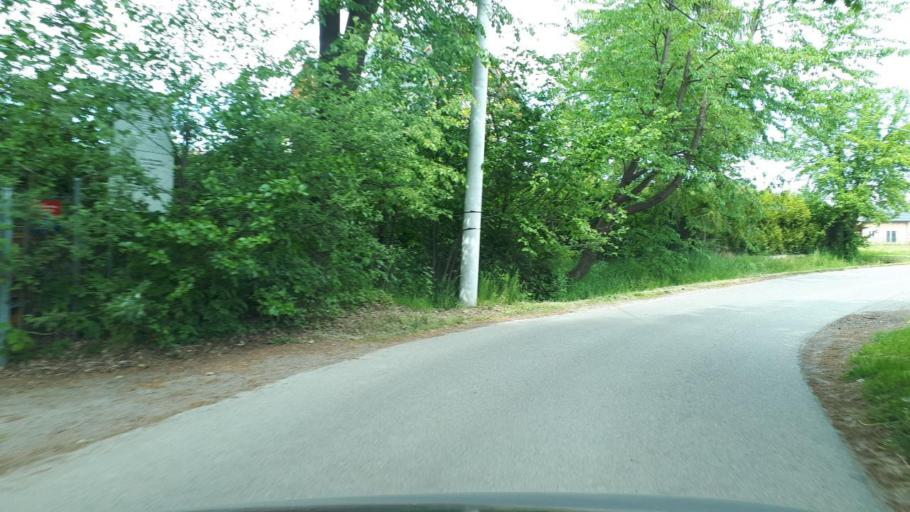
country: PL
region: Silesian Voivodeship
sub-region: Powiat bielski
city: Pisarzowice
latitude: 49.8852
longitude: 19.1323
